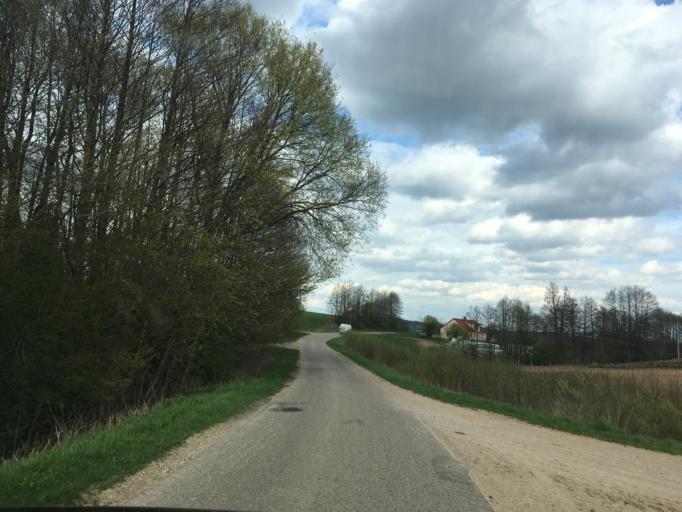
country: PL
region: Podlasie
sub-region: Suwalki
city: Suwalki
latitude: 54.3734
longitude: 22.9353
